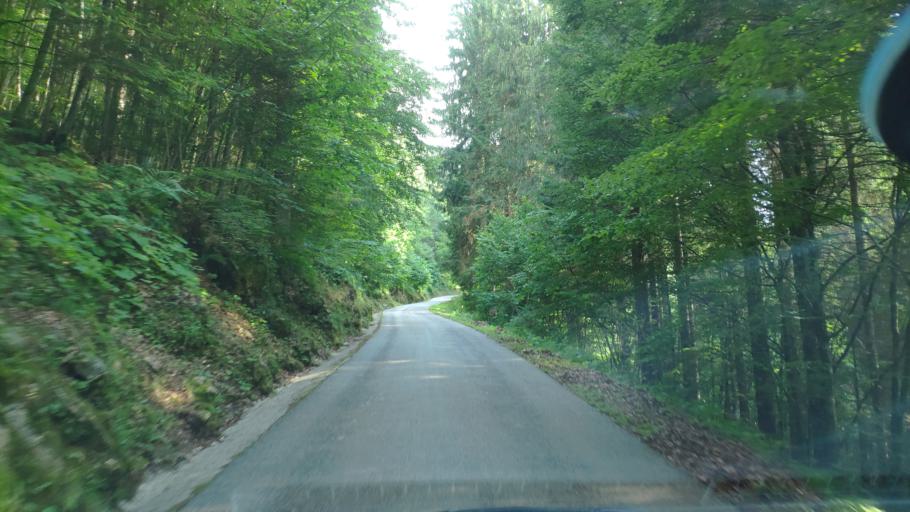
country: IT
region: Veneto
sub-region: Provincia di Vicenza
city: Cogollo del Cengio
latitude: 45.8185
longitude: 11.4382
